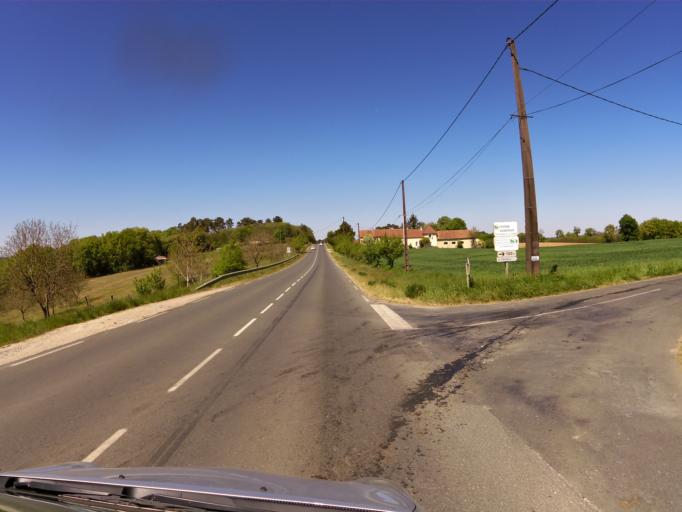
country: FR
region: Aquitaine
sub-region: Departement de la Dordogne
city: Sarlat-la-Caneda
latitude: 44.9757
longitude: 1.2374
